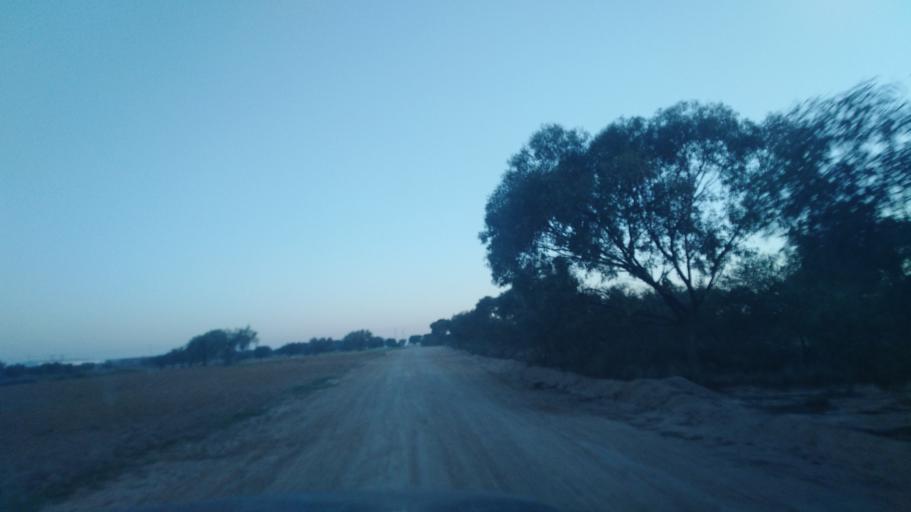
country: TN
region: Safaqis
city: Sfax
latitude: 34.7277
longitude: 10.4465
